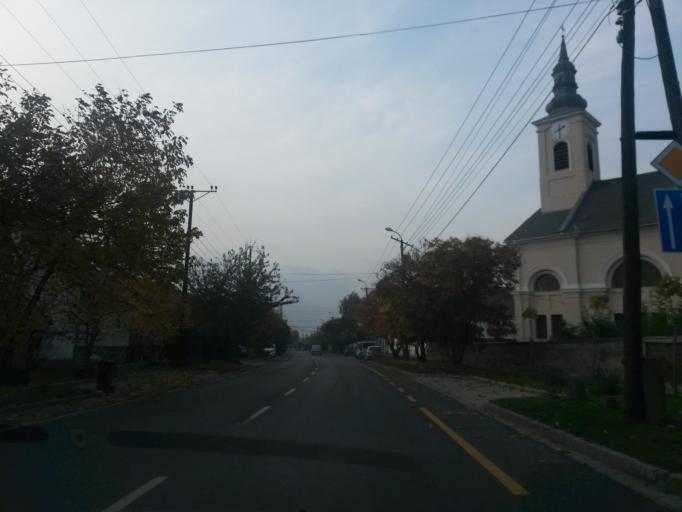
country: HU
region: Gyor-Moson-Sopron
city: Rajka
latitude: 47.9125
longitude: 17.1644
